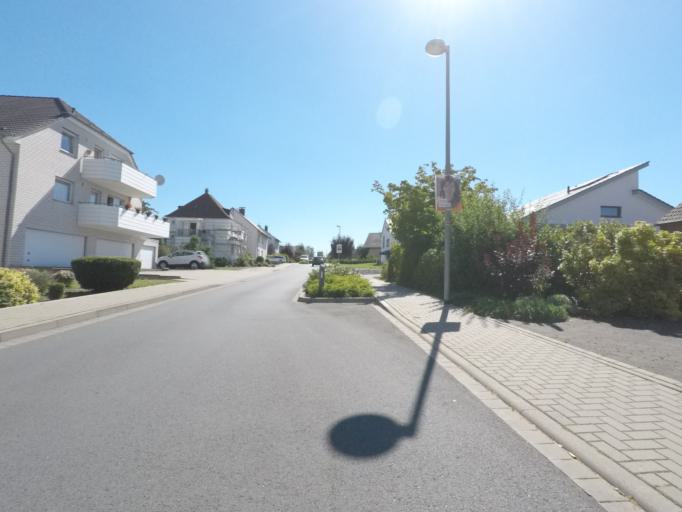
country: DE
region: North Rhine-Westphalia
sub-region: Regierungsbezirk Detmold
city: Herford
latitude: 52.1256
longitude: 8.6379
